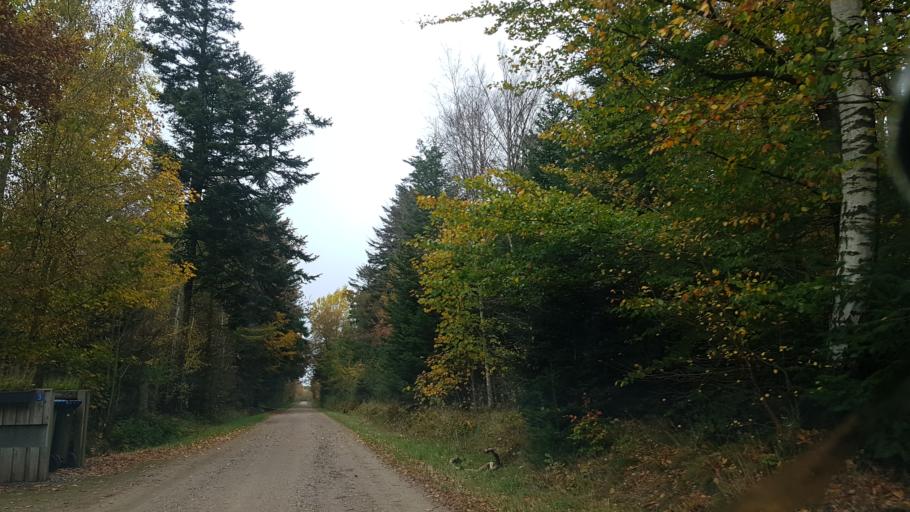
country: DK
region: South Denmark
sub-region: Tonder Kommune
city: Sherrebek
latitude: 55.1853
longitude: 8.7638
